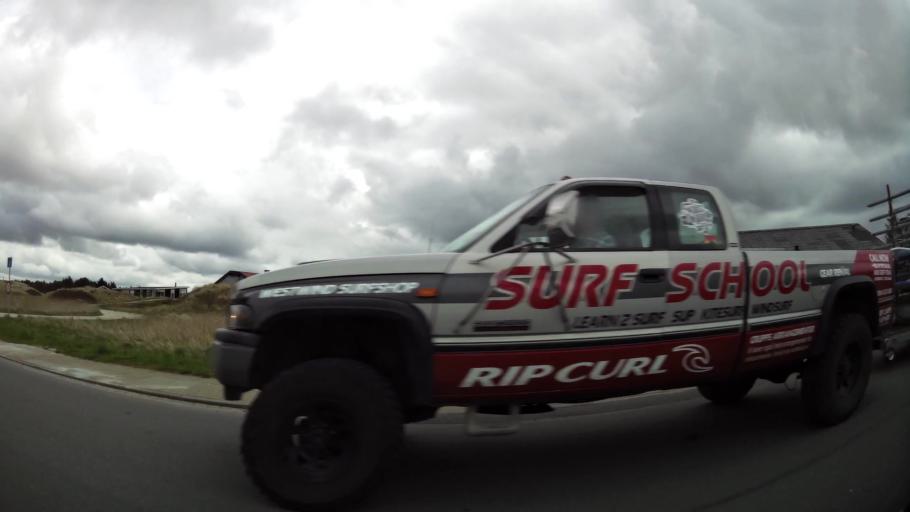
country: DK
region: North Denmark
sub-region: Thisted Kommune
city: Hanstholm
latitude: 57.0399
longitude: 8.4945
